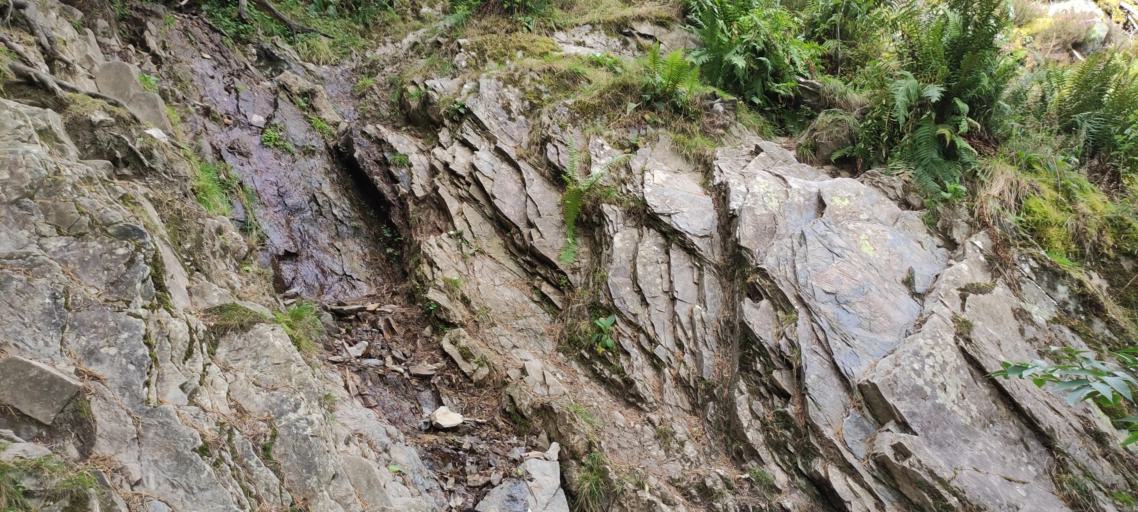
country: GB
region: England
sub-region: Cumbria
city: Keswick
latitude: 54.6268
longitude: -3.2184
